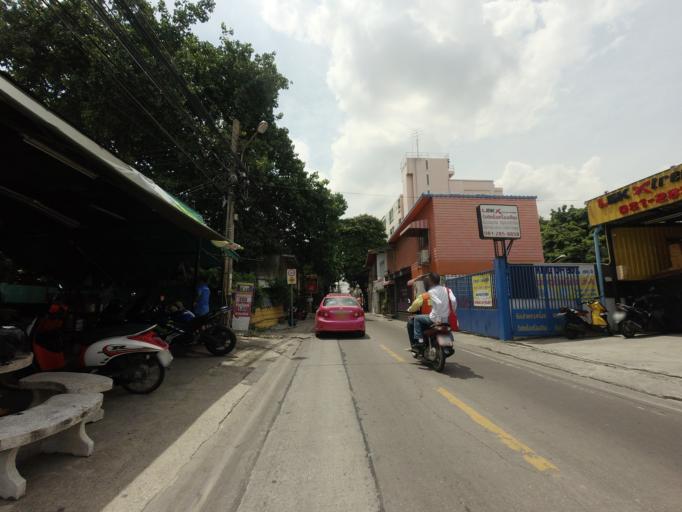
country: TH
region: Bangkok
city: Din Daeng
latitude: 13.7789
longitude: 100.5640
